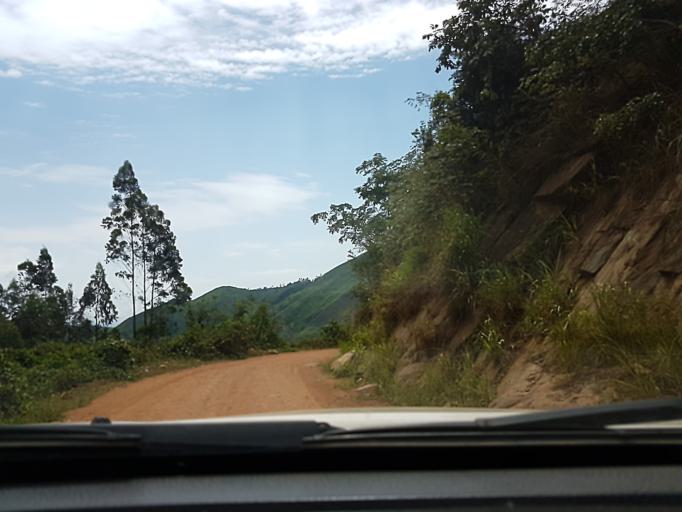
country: RW
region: Western Province
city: Cyangugu
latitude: -2.7048
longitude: 28.9489
